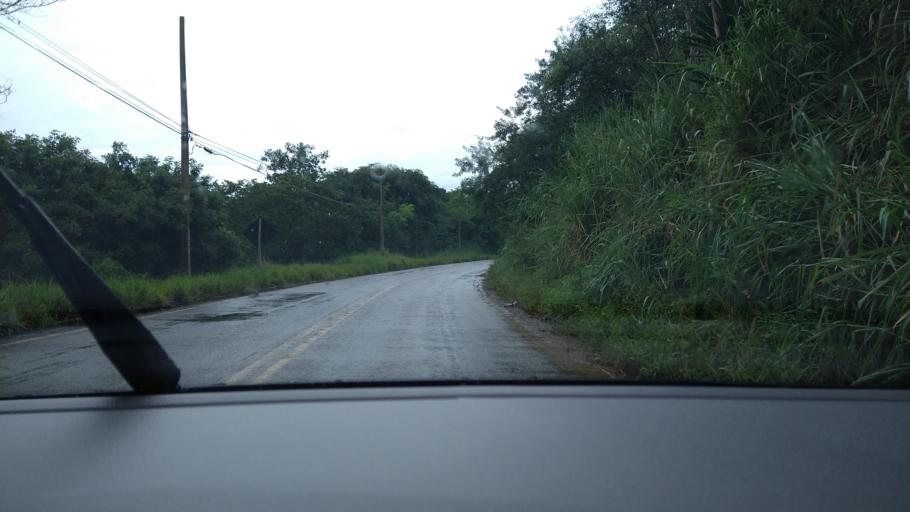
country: BR
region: Minas Gerais
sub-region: Ponte Nova
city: Ponte Nova
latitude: -20.3818
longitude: -42.9023
